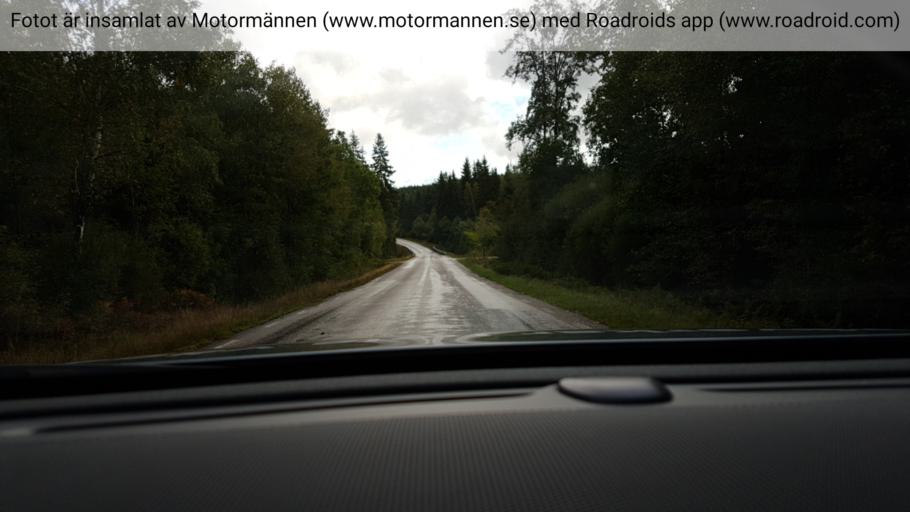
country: SE
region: Vaestra Goetaland
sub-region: Marks Kommun
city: Fritsla
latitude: 57.4214
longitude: 12.9298
